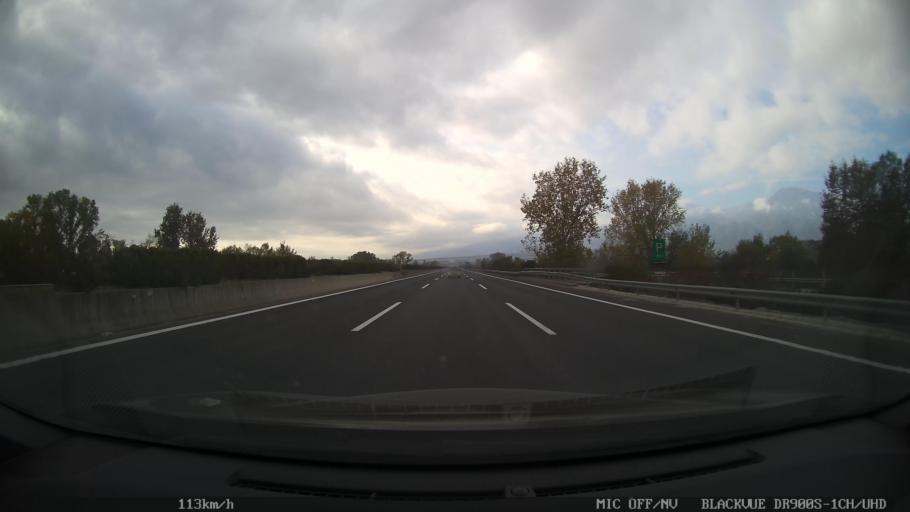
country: GR
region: Central Macedonia
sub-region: Nomos Pierias
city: Dion
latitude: 40.1658
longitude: 22.5460
